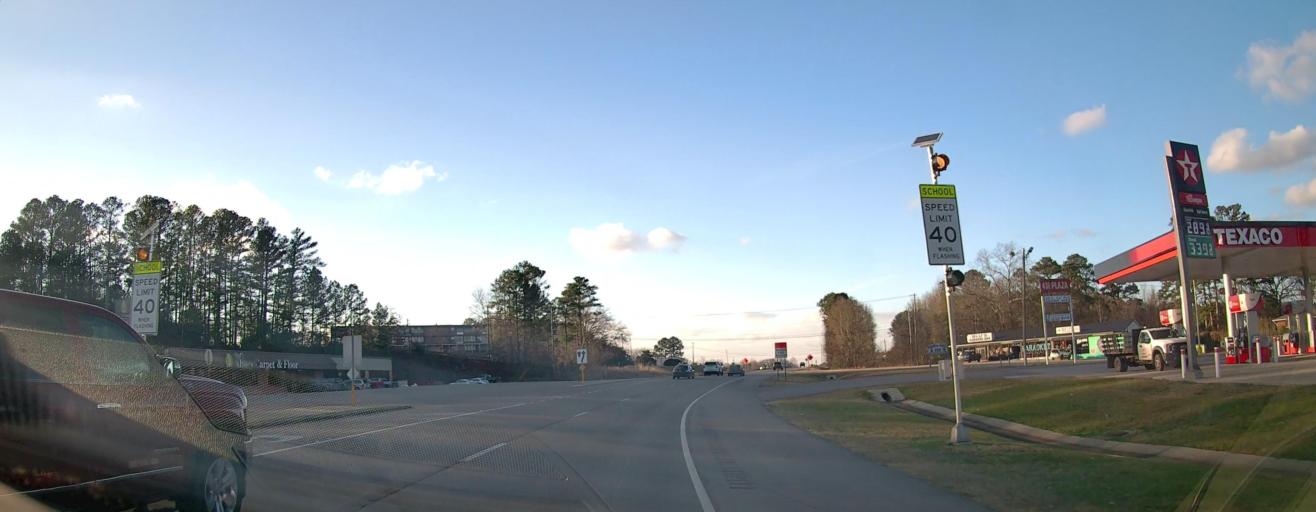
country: US
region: Alabama
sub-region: Calhoun County
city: Saks
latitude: 33.7012
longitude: -85.8291
